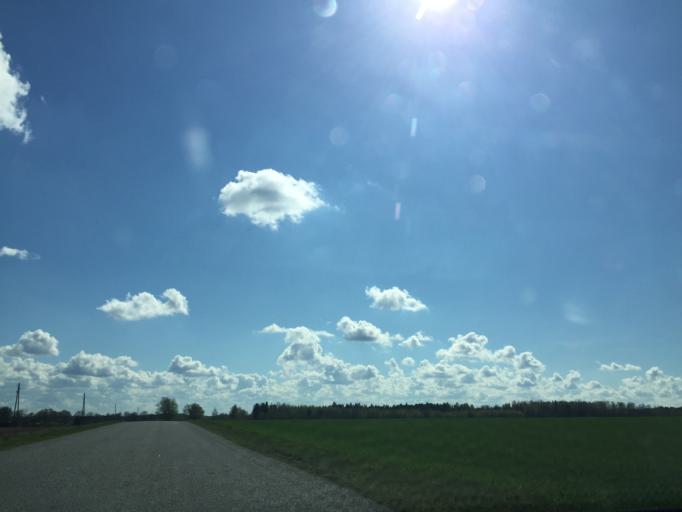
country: LV
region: Strenci
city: Strenci
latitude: 57.5162
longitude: 25.6791
